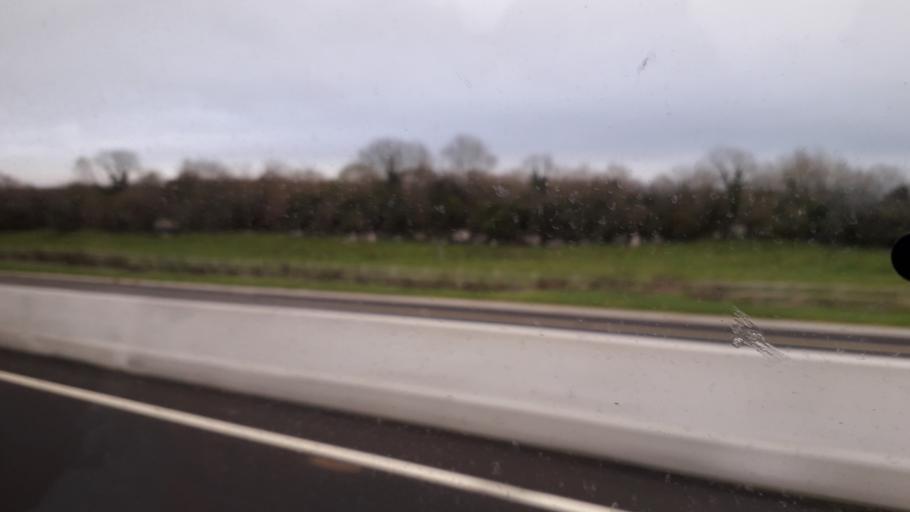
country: IE
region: Connaught
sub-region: County Galway
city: Athenry
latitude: 53.2665
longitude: -8.8129
